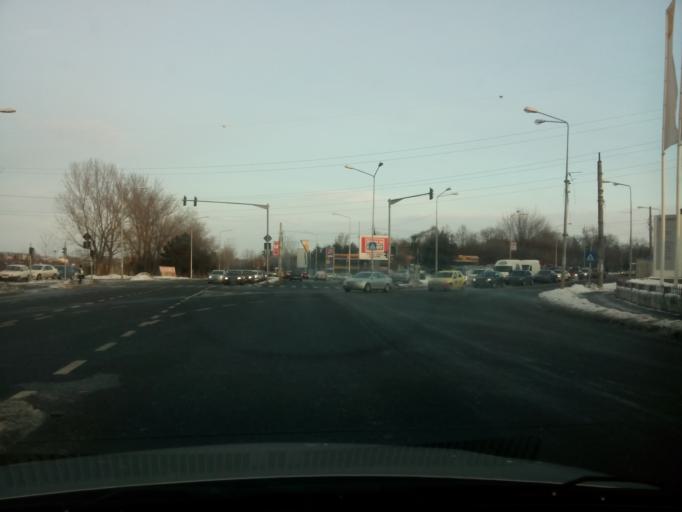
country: RO
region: Ilfov
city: Dobroesti
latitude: 44.4411
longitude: 26.1908
